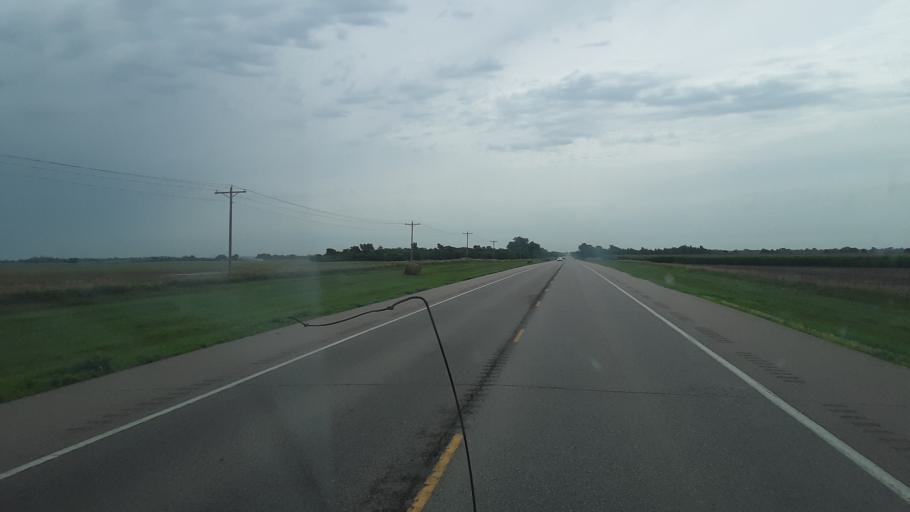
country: US
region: Kansas
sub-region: Stafford County
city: Saint John
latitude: 37.9560
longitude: -98.8576
